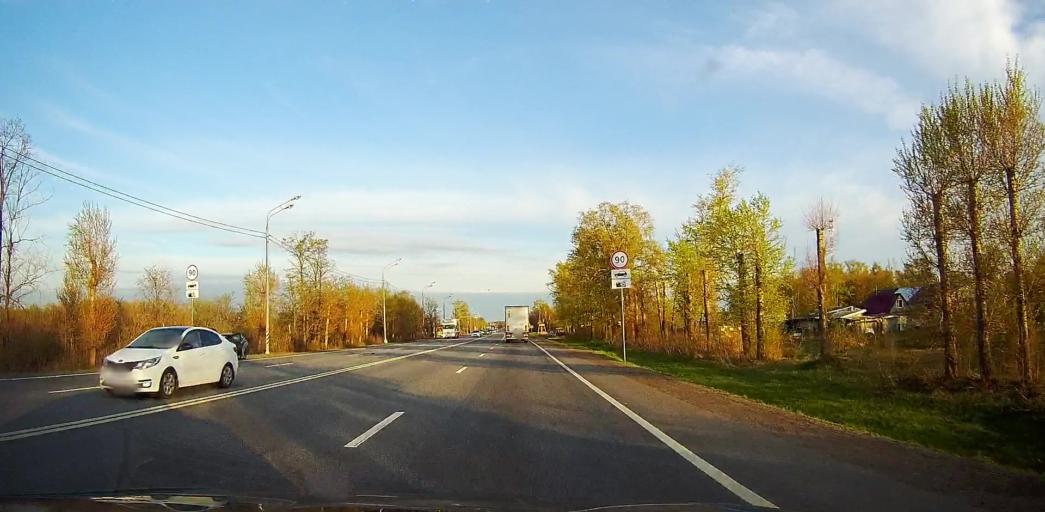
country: RU
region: Moskovskaya
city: Troitskoye
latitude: 55.2644
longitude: 38.5063
